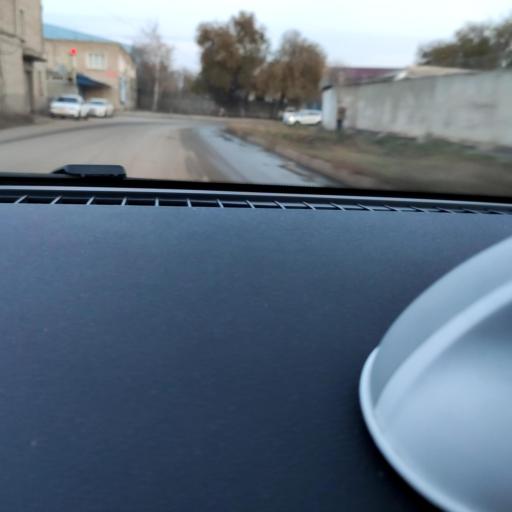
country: RU
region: Samara
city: Samara
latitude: 53.2017
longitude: 50.2542
